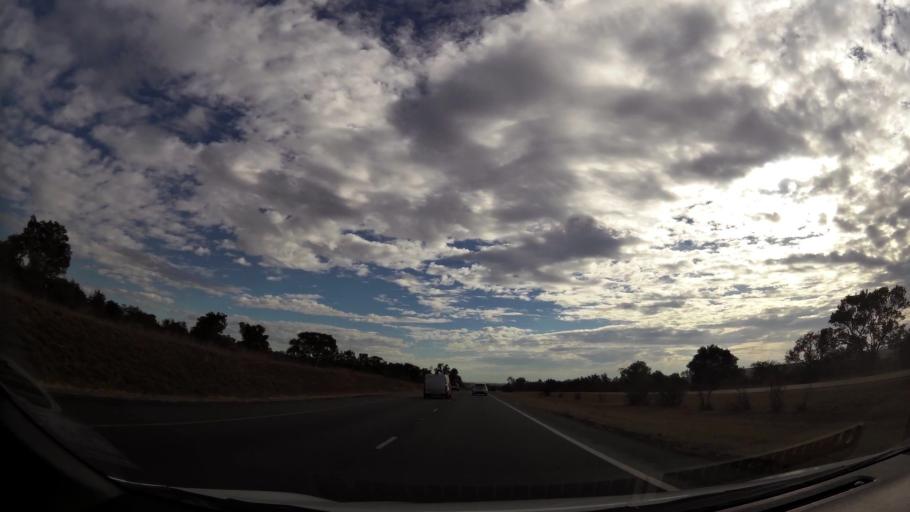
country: ZA
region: Gauteng
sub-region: City of Tshwane Metropolitan Municipality
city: Mabopane
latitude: -25.4629
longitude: 28.2945
